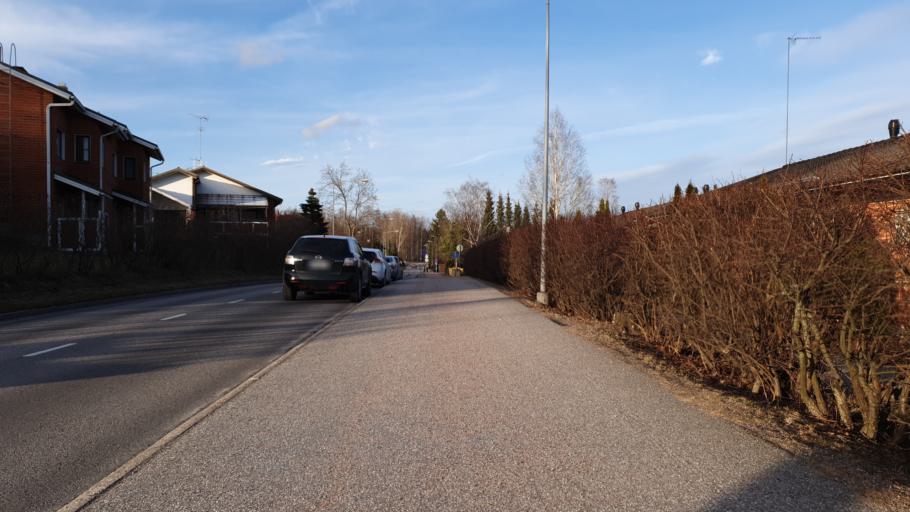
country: FI
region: Uusimaa
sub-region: Helsinki
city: Vantaa
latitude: 60.3100
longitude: 25.0065
